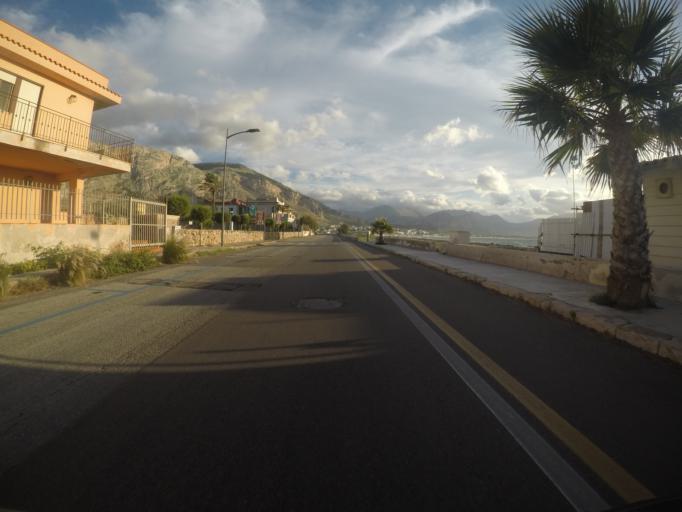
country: IT
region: Sicily
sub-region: Palermo
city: Isola delle Femmine
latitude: 38.1971
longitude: 13.2437
